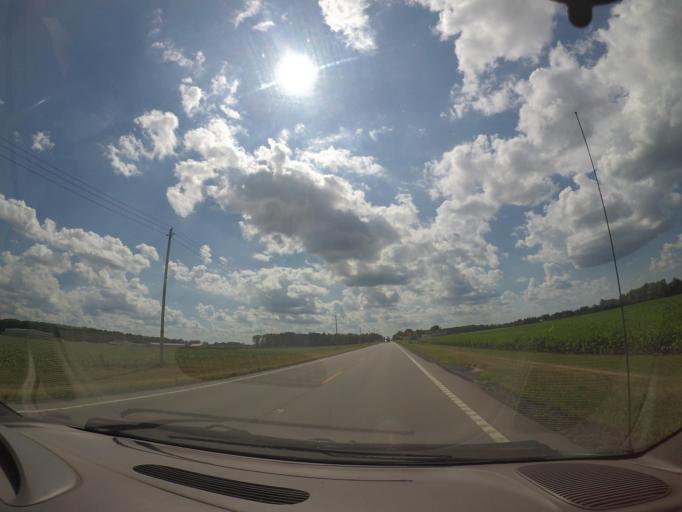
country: US
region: Ohio
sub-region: Huron County
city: Norwalk
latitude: 41.2494
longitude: -82.5520
